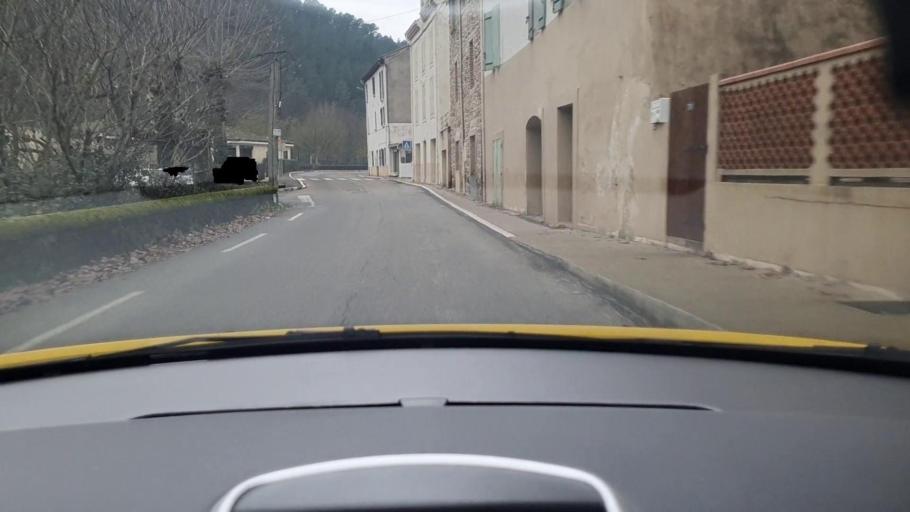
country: FR
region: Languedoc-Roussillon
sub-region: Departement du Gard
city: Besseges
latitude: 44.2802
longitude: 4.1021
